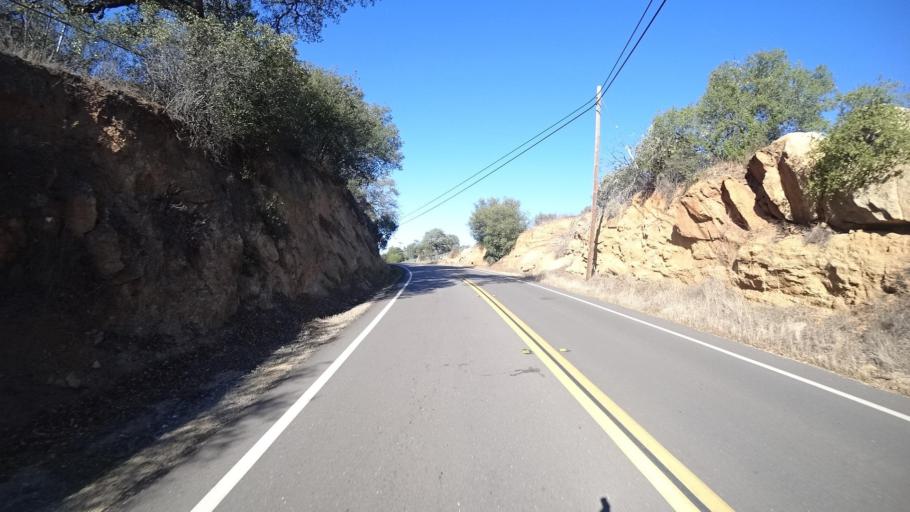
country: US
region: California
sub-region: San Diego County
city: Jamul
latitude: 32.6762
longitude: -116.7327
